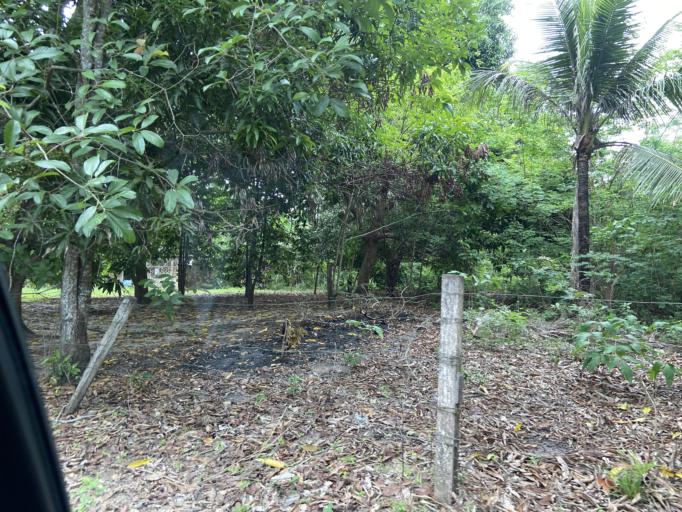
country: BR
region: Para
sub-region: Maraba
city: Maraba
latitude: -5.2940
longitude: -49.0633
